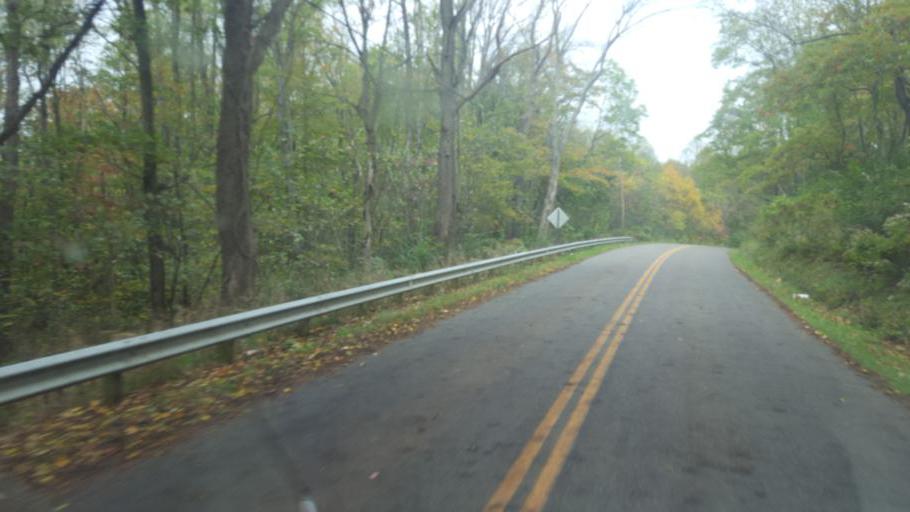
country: US
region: Ohio
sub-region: Carroll County
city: Carrollton
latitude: 40.4942
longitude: -81.1529
